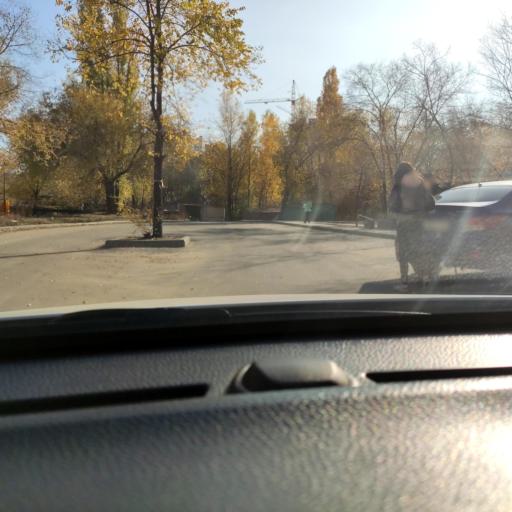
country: RU
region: Voronezj
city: Voronezh
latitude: 51.7218
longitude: 39.2611
